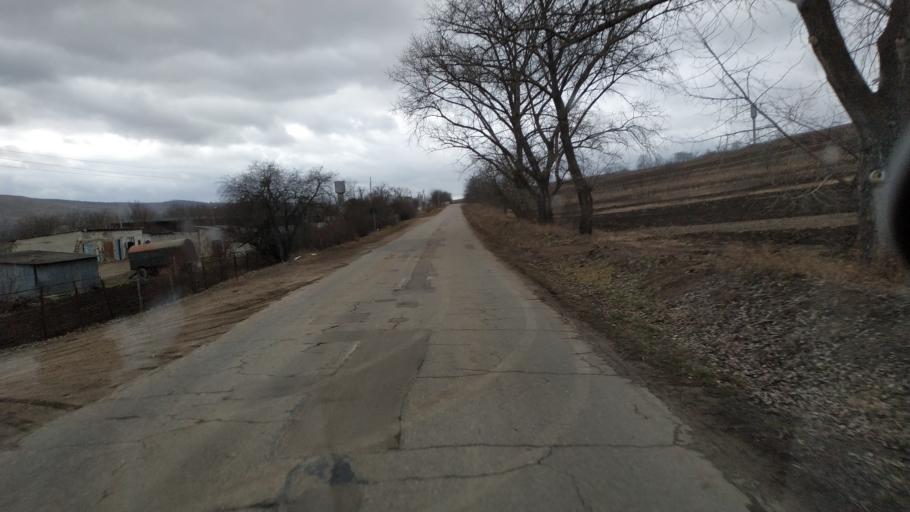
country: MD
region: Calarasi
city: Calarasi
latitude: 47.2422
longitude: 28.2207
